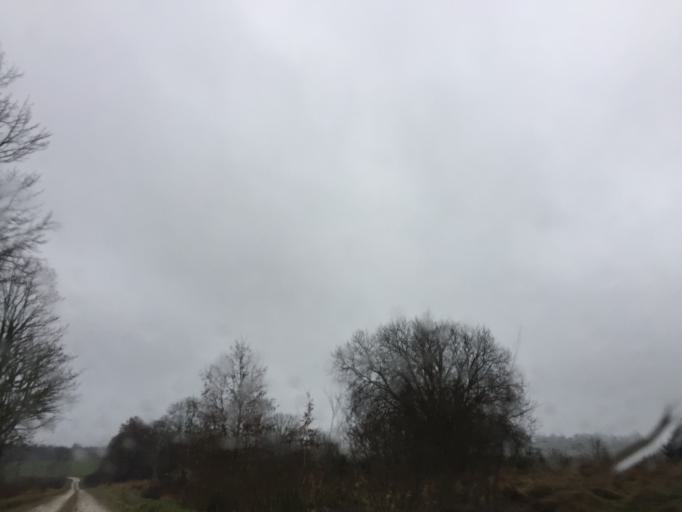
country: LV
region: Viesite
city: Viesite
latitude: 56.4482
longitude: 25.6298
